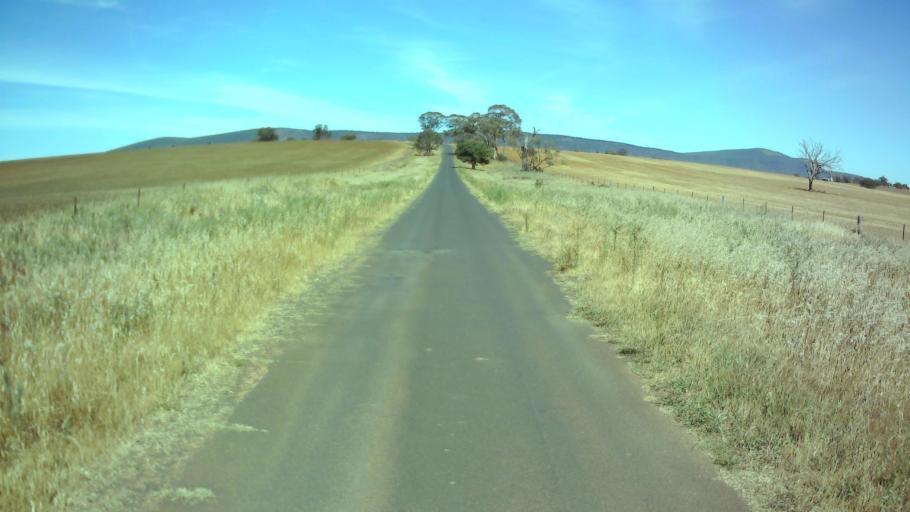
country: AU
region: New South Wales
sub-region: Weddin
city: Grenfell
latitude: -33.9405
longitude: 148.0740
